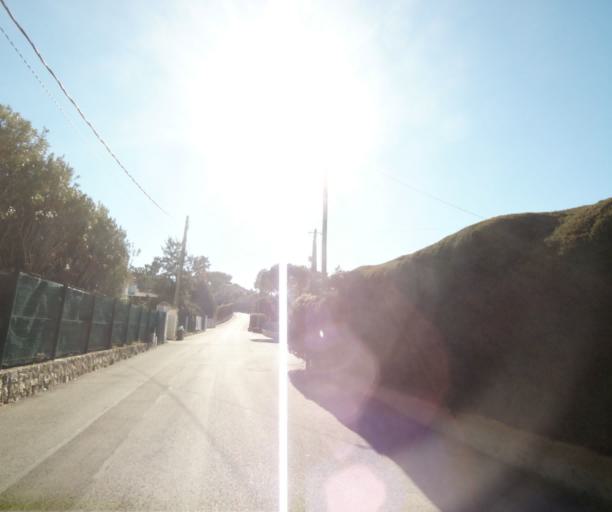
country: FR
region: Provence-Alpes-Cote d'Azur
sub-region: Departement des Alpes-Maritimes
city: Antibes
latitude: 43.5523
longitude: 7.1257
